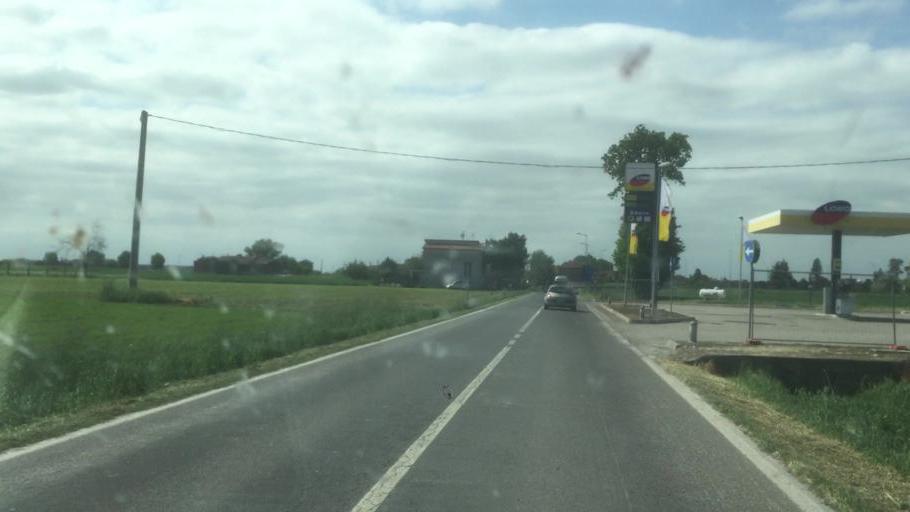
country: IT
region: Veneto
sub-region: Provincia di Rovigo
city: Ceneselli
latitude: 45.0113
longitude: 11.3762
